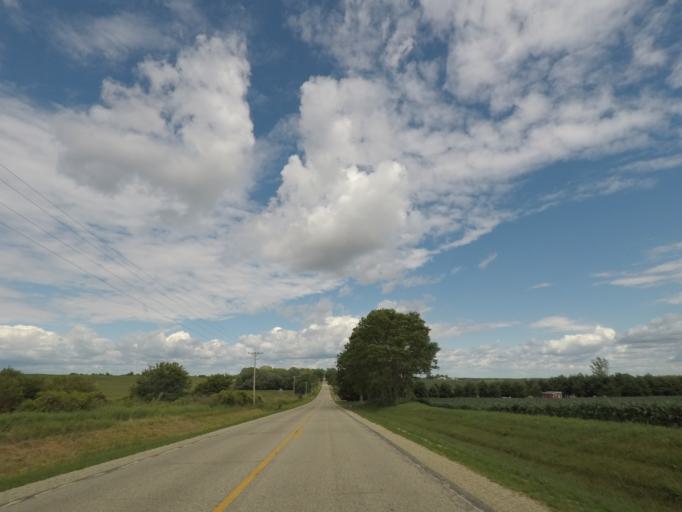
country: US
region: Wisconsin
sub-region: Rock County
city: Orfordville
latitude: 42.7130
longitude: -89.2160
